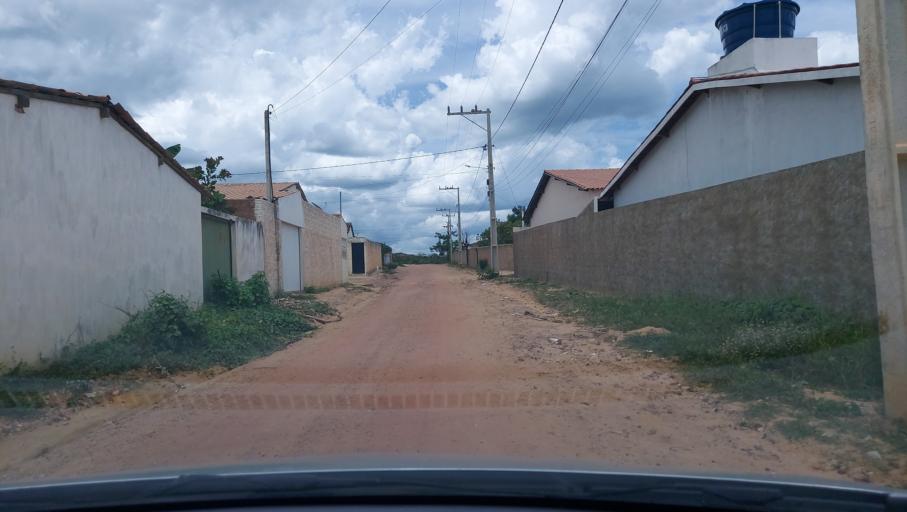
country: BR
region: Bahia
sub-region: Oliveira Dos Brejinhos
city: Beira Rio
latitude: -12.0052
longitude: -42.6319
